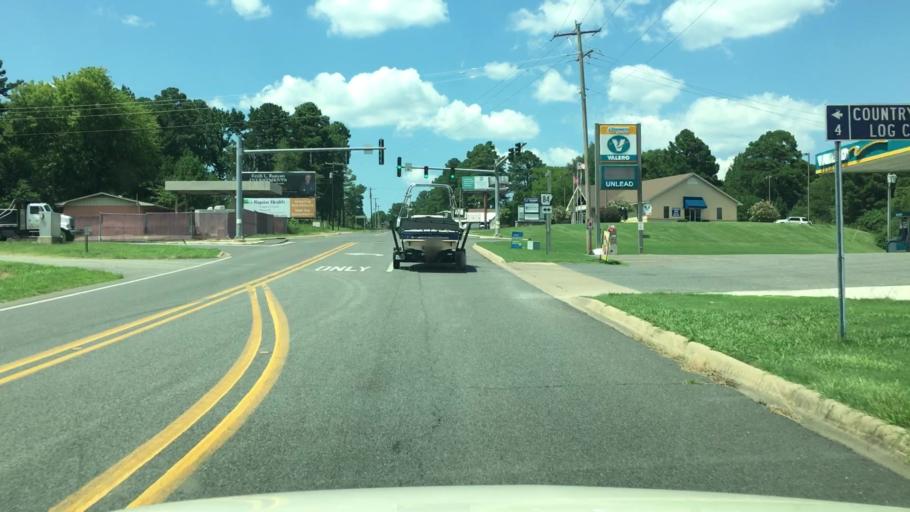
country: US
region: Arkansas
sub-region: Garland County
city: Lake Hamilton
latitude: 34.3159
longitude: -93.1707
